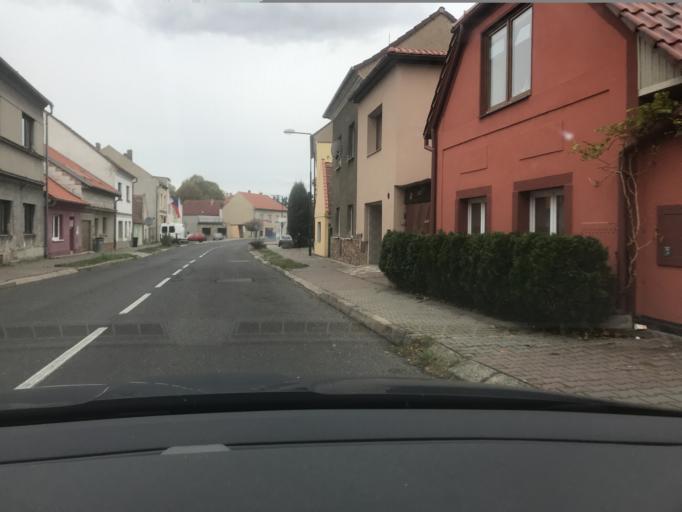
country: CZ
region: Ustecky
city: Trebenice
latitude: 50.4778
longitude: 13.9953
